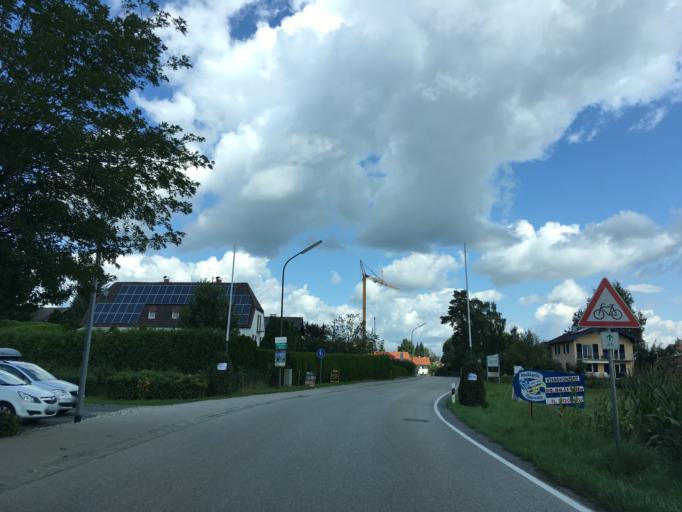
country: DE
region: Bavaria
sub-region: Upper Bavaria
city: Eggstatt
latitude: 47.9202
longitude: 12.3805
